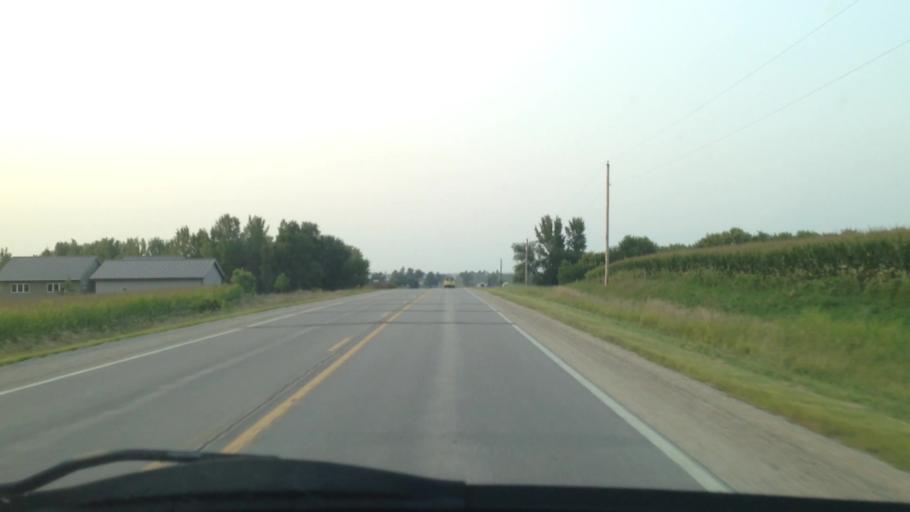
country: US
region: Iowa
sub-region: Benton County
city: Atkins
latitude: 41.9965
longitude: -91.8733
